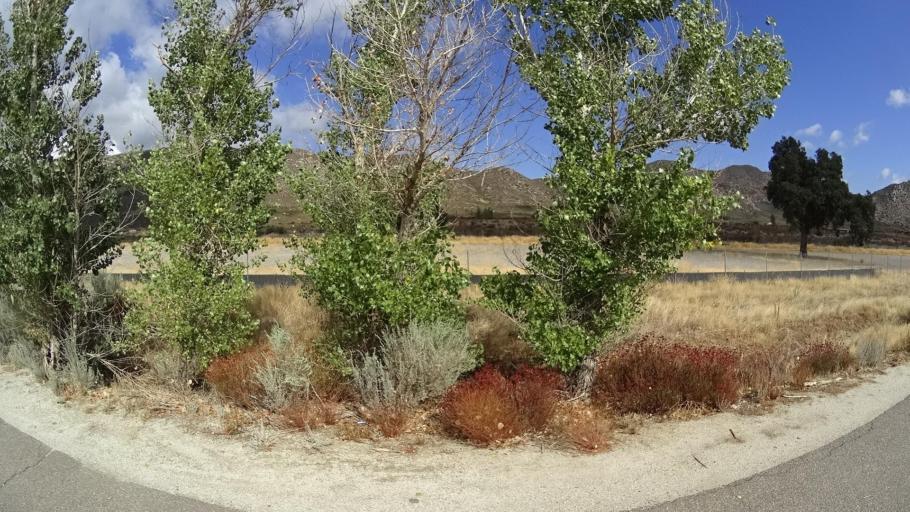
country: US
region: California
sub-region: San Diego County
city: Pine Valley
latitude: 32.7615
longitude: -116.4883
